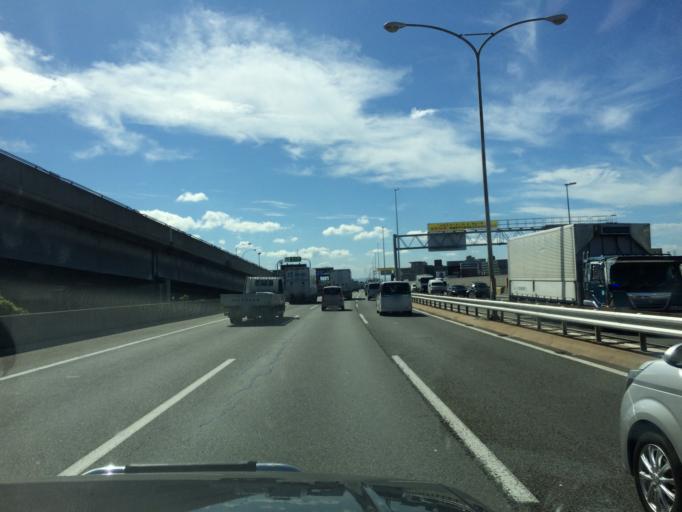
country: JP
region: Osaka
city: Daitocho
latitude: 34.6759
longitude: 135.5978
